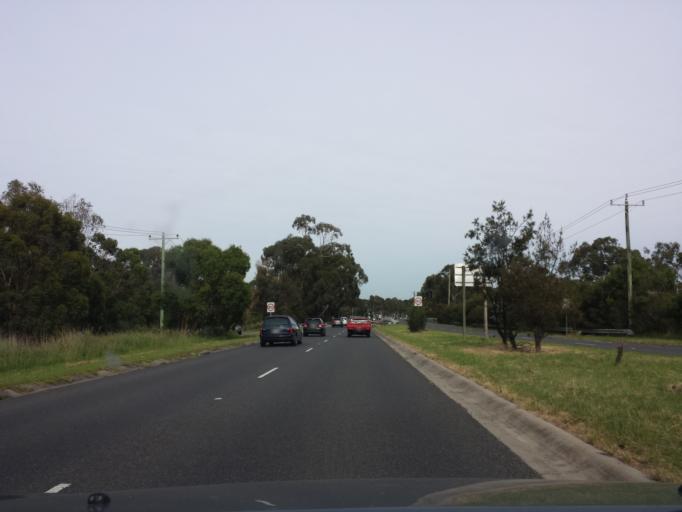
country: AU
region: Victoria
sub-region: Whitehorse
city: Vermont South
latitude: -37.8769
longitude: 145.1931
